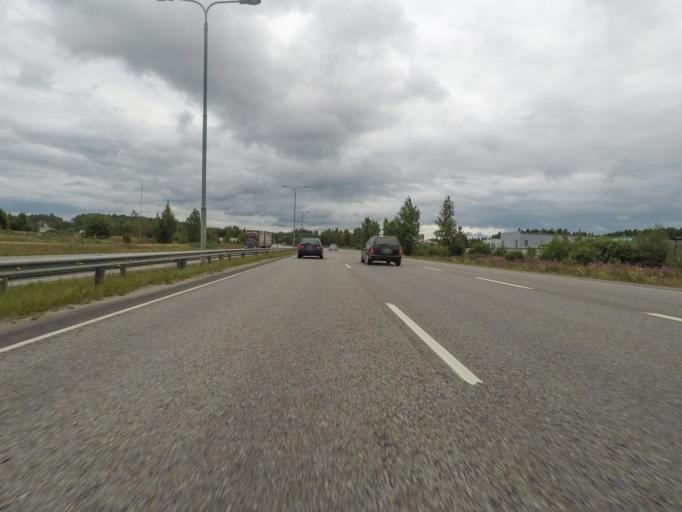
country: FI
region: Varsinais-Suomi
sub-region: Turku
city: Turku
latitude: 60.4865
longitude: 22.3204
